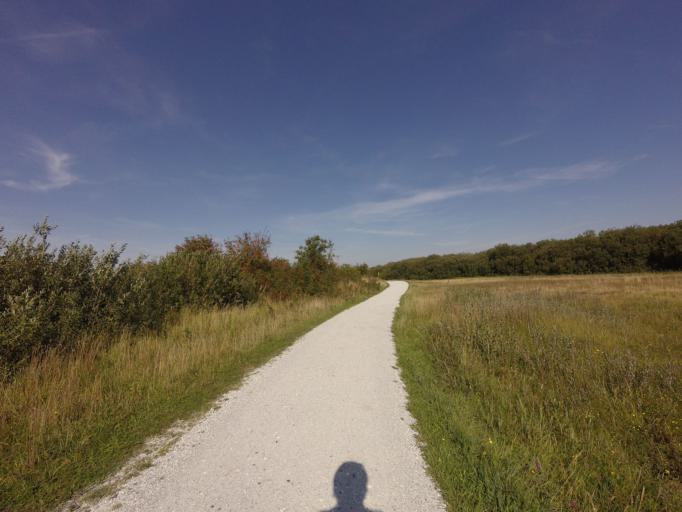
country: NL
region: Friesland
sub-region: Gemeente Schiermonnikoog
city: Schiermonnikoog
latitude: 53.4713
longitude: 6.1467
